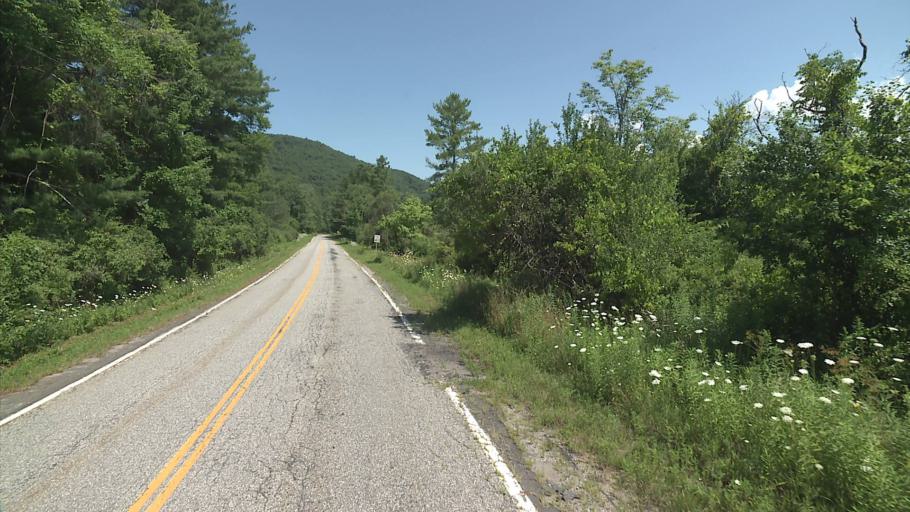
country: US
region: Connecticut
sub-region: Litchfield County
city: Canaan
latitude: 41.9023
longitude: -73.2805
